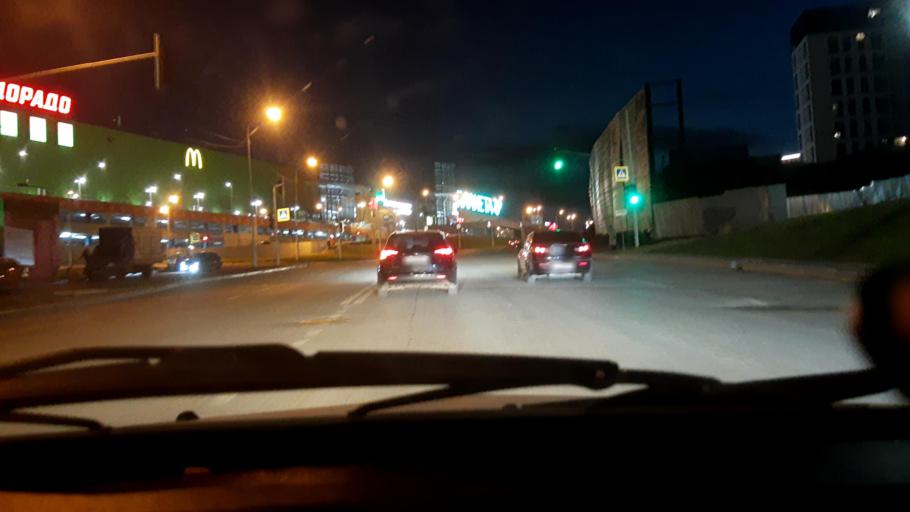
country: RU
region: Bashkortostan
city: Ufa
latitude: 54.7603
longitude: 56.0374
